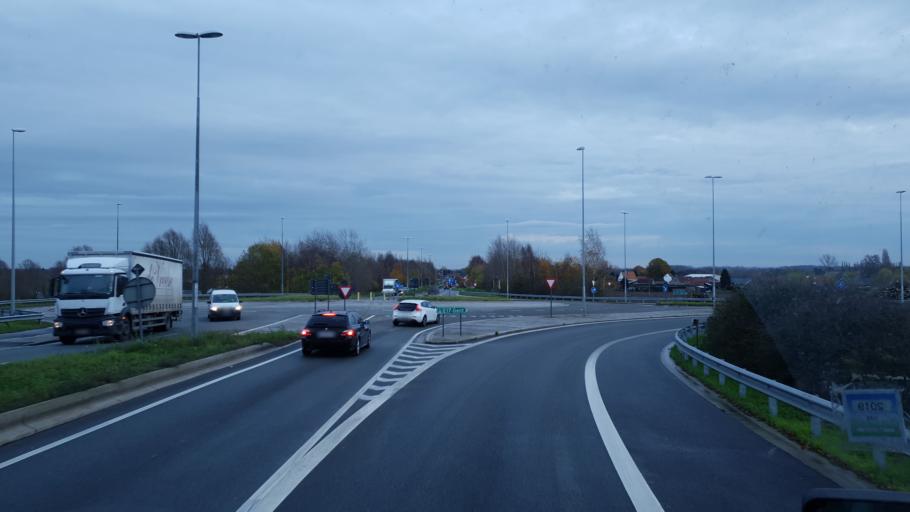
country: BE
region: Flanders
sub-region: Provincie Oost-Vlaanderen
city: Nazareth
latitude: 50.9549
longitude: 3.5654
